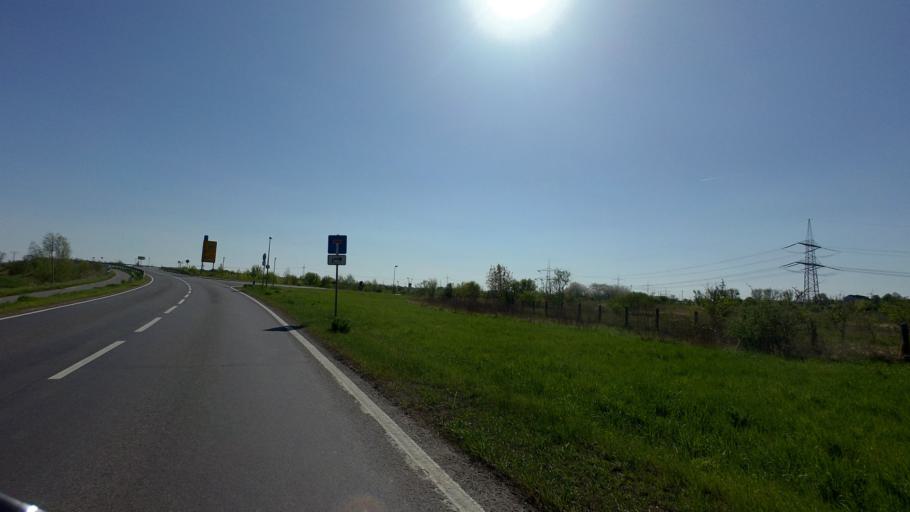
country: DE
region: Brandenburg
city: Wustermark
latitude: 52.5592
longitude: 12.9532
